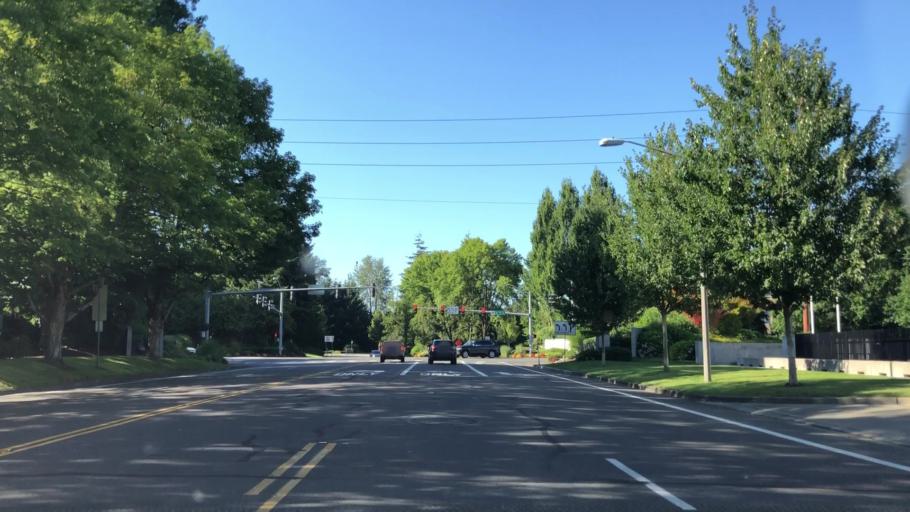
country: US
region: Washington
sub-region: King County
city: Bothell
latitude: 47.7683
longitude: -122.1849
